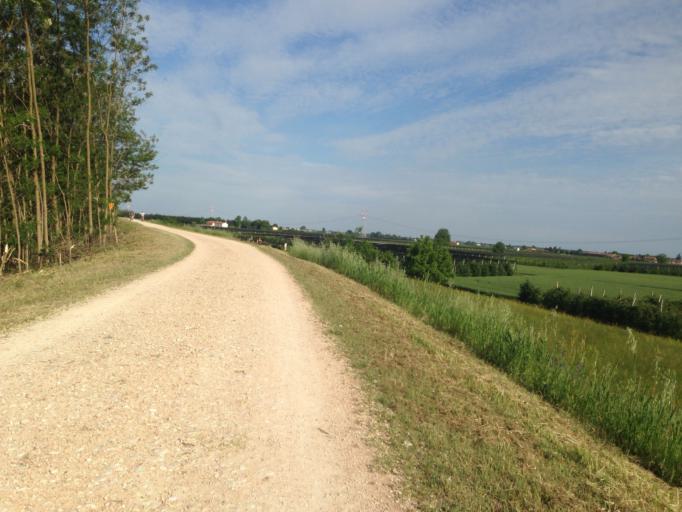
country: IT
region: Veneto
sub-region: Provincia di Verona
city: Zevio
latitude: 45.3719
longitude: 11.1541
